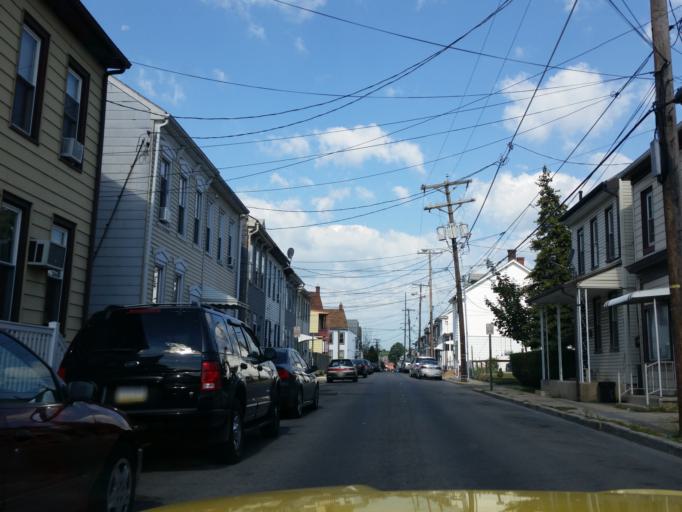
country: US
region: Pennsylvania
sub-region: Lebanon County
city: Lebanon
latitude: 40.3477
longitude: -76.4160
